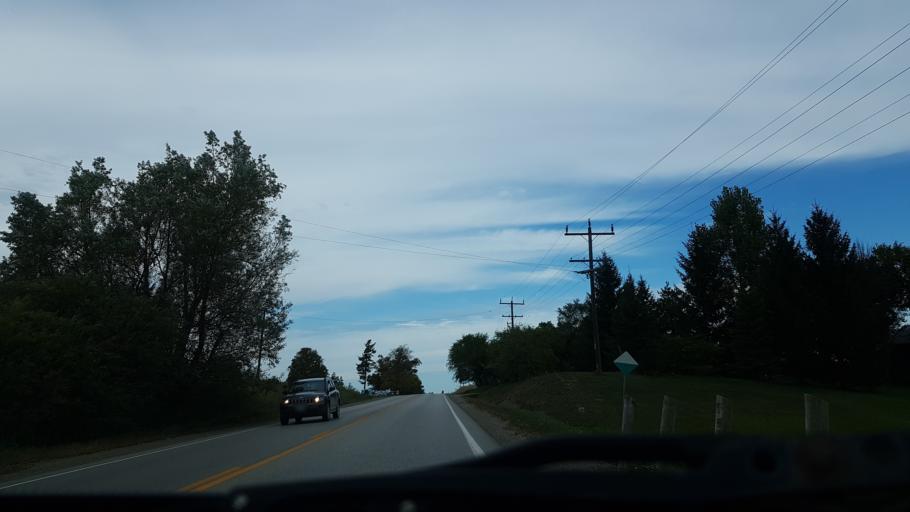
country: CA
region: Ontario
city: Wasaga Beach
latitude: 44.3790
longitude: -80.0874
